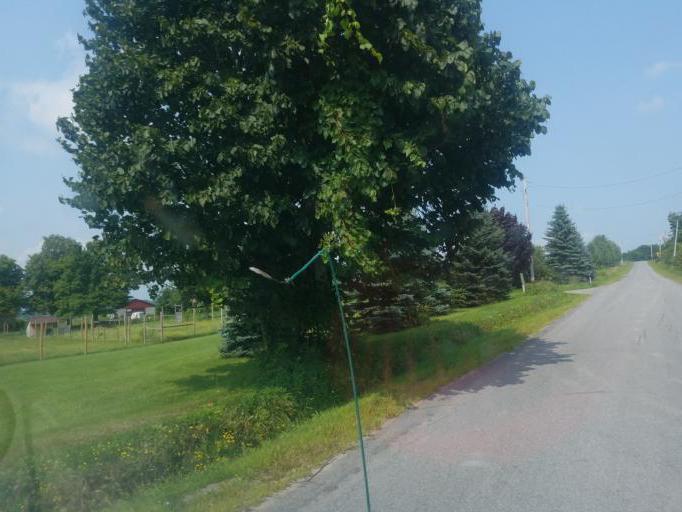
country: US
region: New York
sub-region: Montgomery County
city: Wellsville
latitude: 42.8633
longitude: -74.3283
